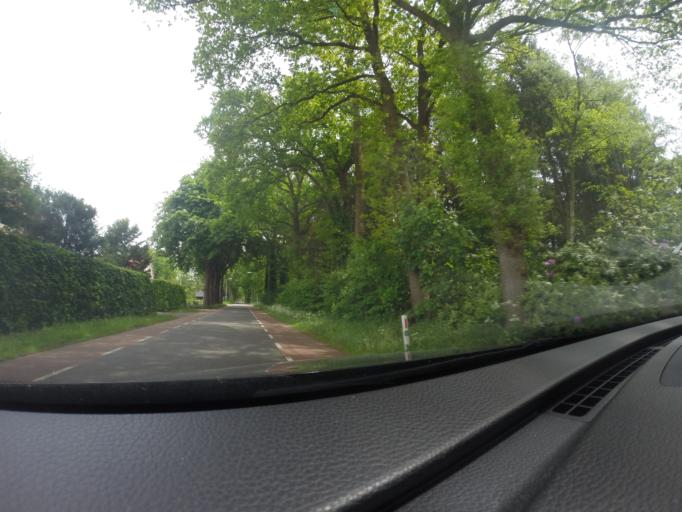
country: NL
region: Gelderland
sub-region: Gemeente Lochem
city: Eefde
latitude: 52.1598
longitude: 6.2514
